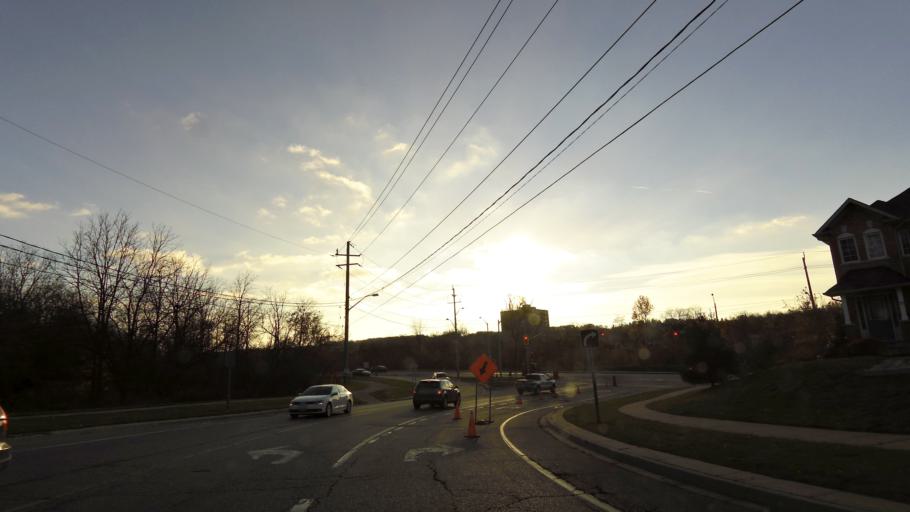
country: CA
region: Ontario
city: Cambridge
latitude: 43.3508
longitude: -80.3137
